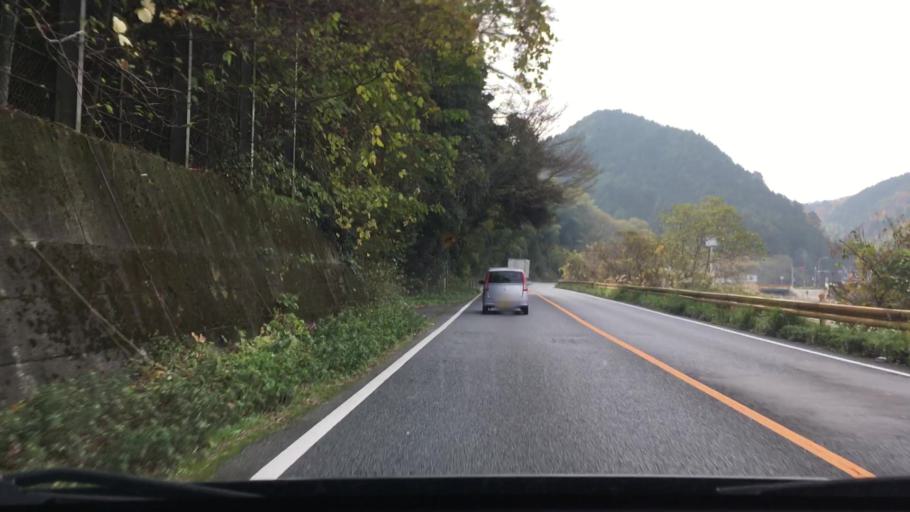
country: JP
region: Yamaguchi
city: Iwakuni
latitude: 34.1301
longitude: 132.1460
